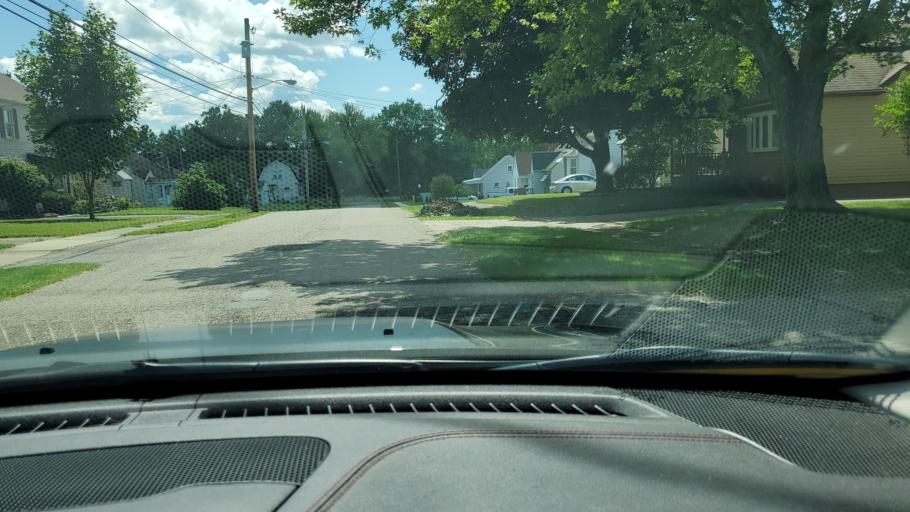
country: US
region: Ohio
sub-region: Trumbull County
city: Niles
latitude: 41.1823
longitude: -80.7800
